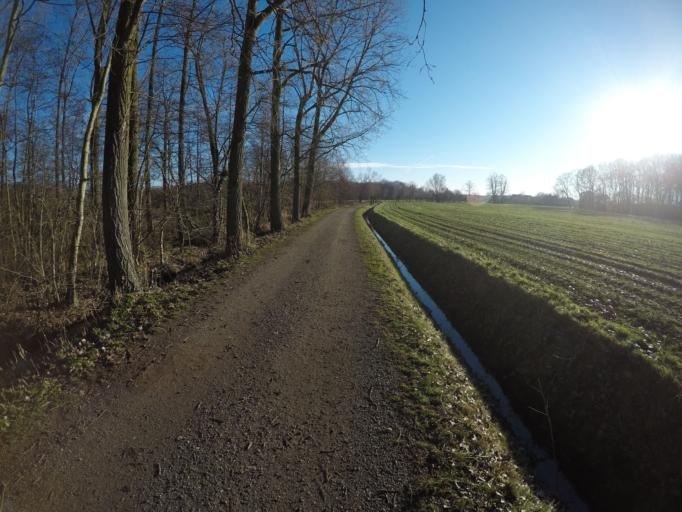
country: BE
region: Flanders
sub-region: Provincie Antwerpen
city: Schilde
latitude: 51.2202
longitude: 4.5890
